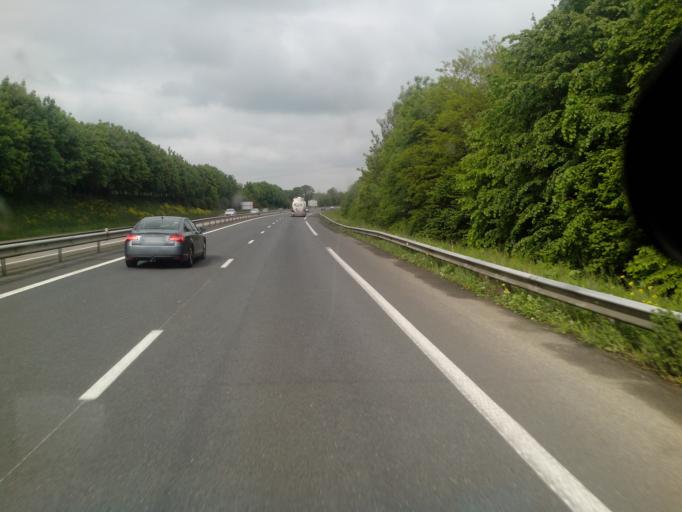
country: FR
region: Lower Normandy
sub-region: Departement du Calvados
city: Villers-Bocage
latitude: 49.1024
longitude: -0.6110
